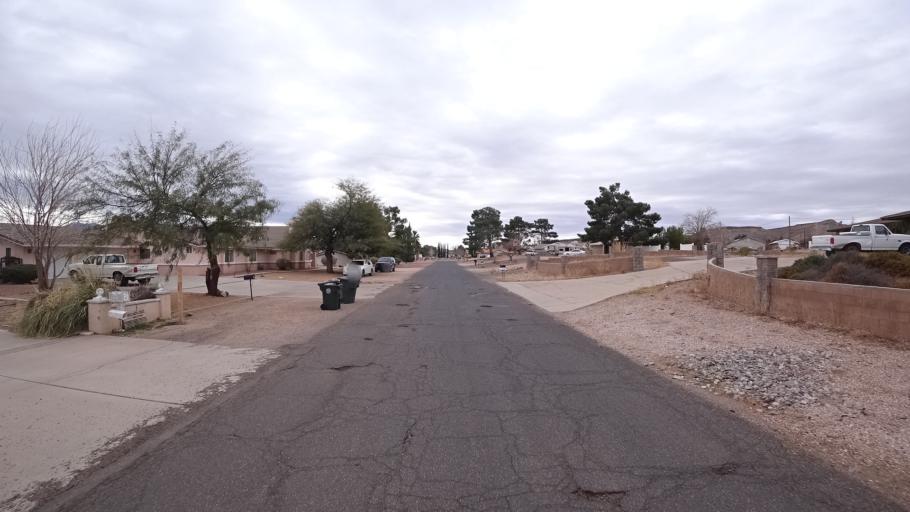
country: US
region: Arizona
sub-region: Mohave County
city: New Kingman-Butler
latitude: 35.2354
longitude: -114.0460
